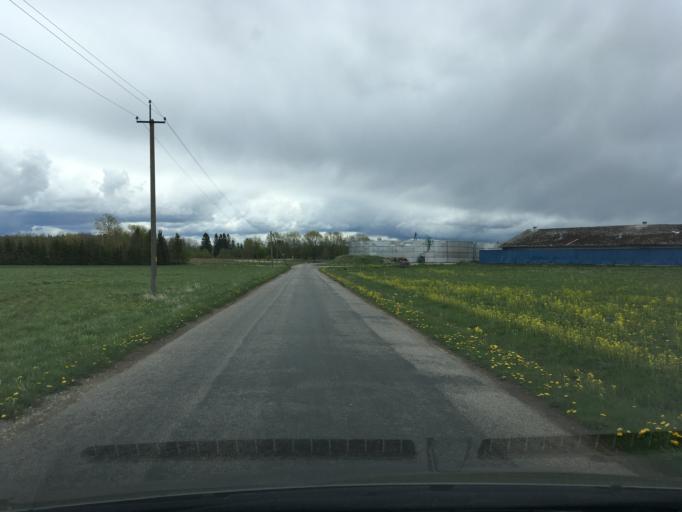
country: EE
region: Harju
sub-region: Joelaehtme vald
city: Loo
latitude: 59.3662
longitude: 24.9675
